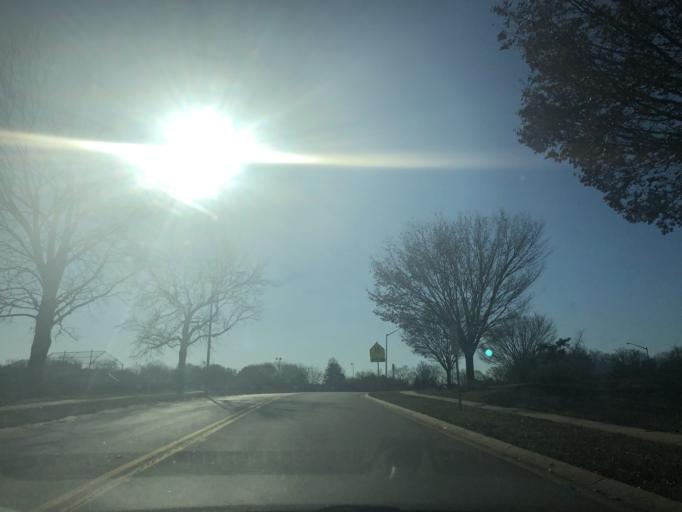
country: US
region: Maryland
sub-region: Howard County
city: Columbia
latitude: 39.2094
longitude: -76.8449
